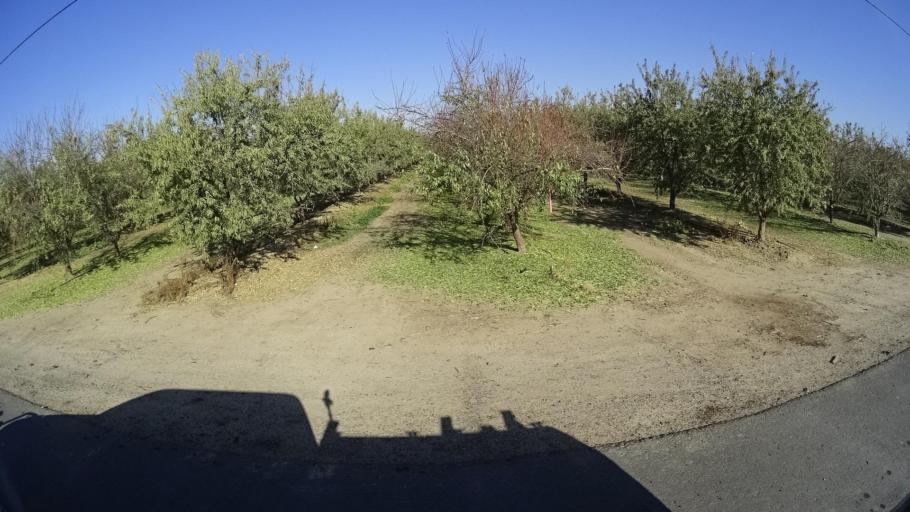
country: US
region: California
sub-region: Kern County
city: Delano
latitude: 35.7178
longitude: -119.3149
